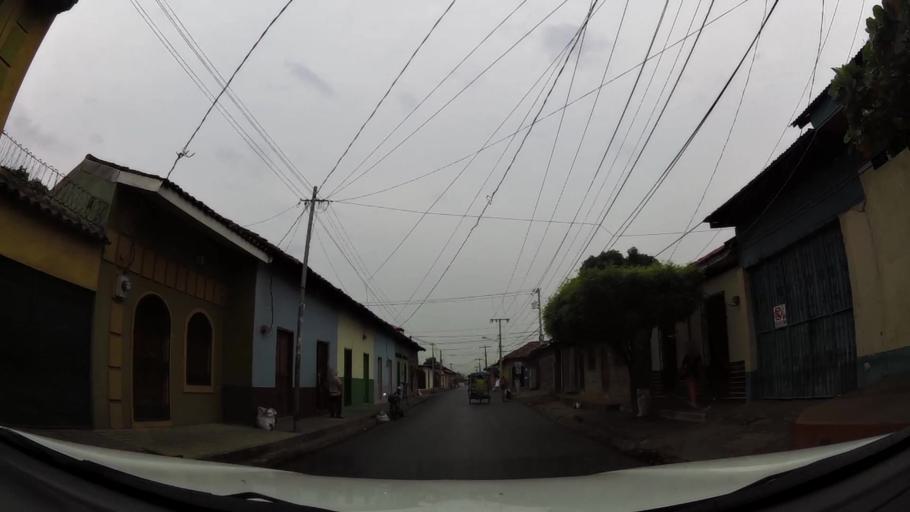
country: NI
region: Leon
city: Leon
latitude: 12.4441
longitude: -86.8765
